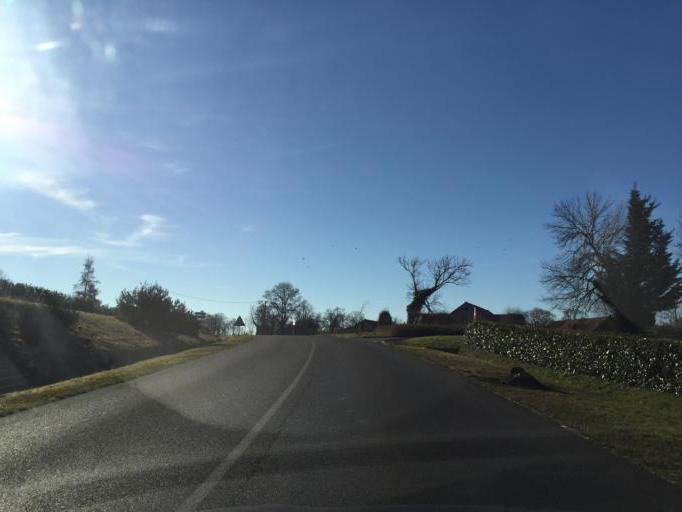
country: FR
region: Auvergne
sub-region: Departement de l'Allier
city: Vendat
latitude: 46.2231
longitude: 3.3425
